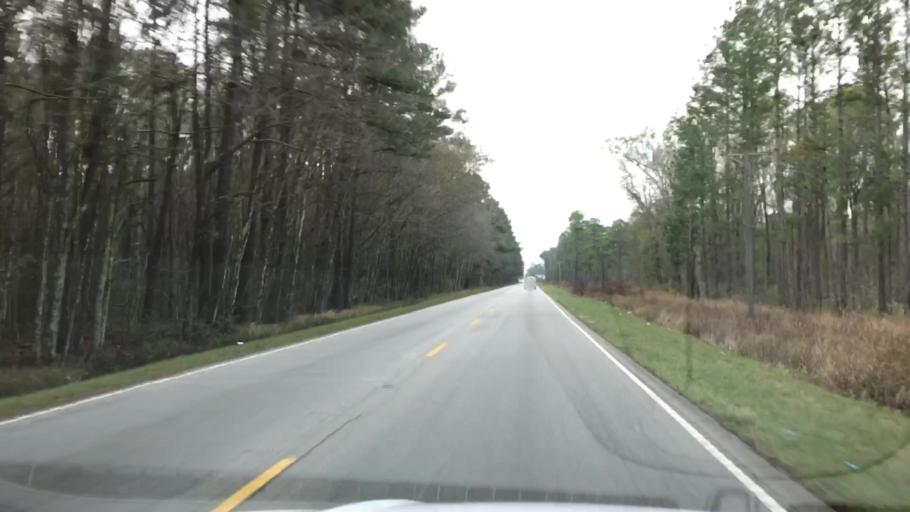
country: US
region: South Carolina
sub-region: Jasper County
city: Ridgeland
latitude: 32.3642
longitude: -80.9183
